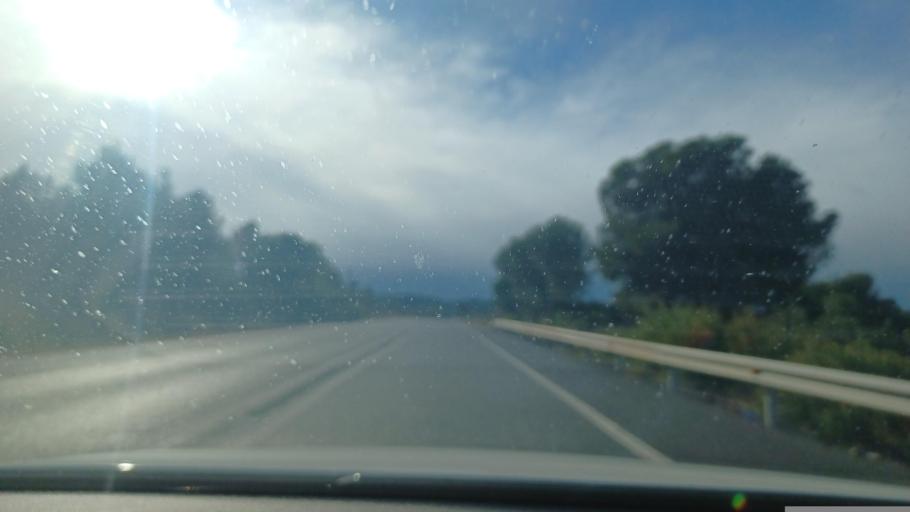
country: ES
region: Catalonia
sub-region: Provincia de Tarragona
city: El Perello
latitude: 40.8915
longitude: 0.7249
